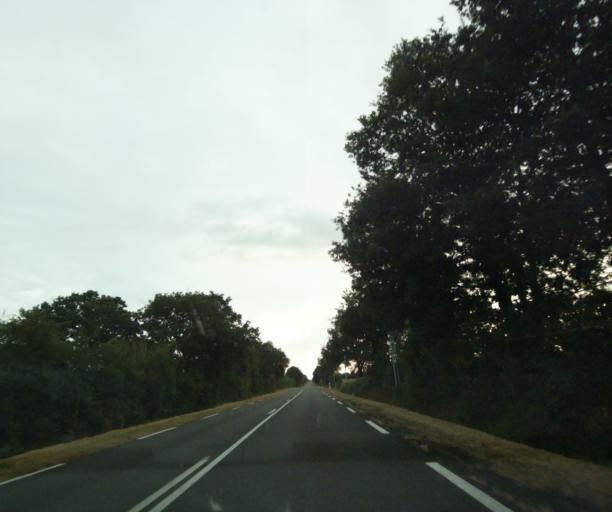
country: FR
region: Pays de la Loire
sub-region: Departement de la Vendee
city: Saint-Hilaire-de-Talmont
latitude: 46.4680
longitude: -1.5818
